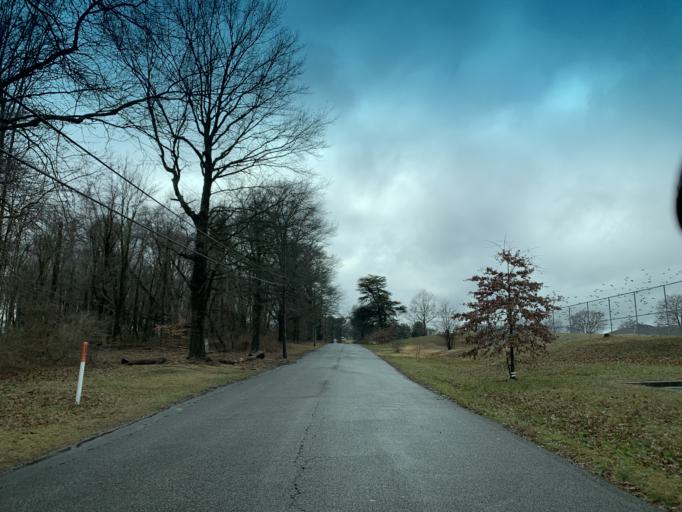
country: US
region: Maryland
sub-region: Harford County
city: Edgewood
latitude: 39.4228
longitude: -76.2988
